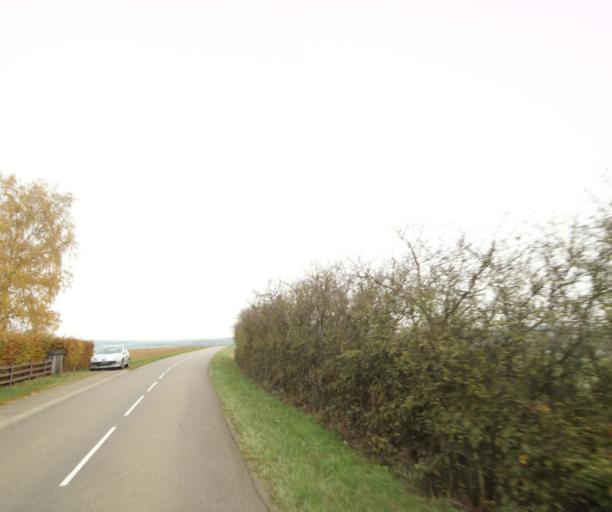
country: FR
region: Lorraine
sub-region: Departement de Meurthe-et-Moselle
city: Mancieulles
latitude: 49.2787
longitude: 5.8802
